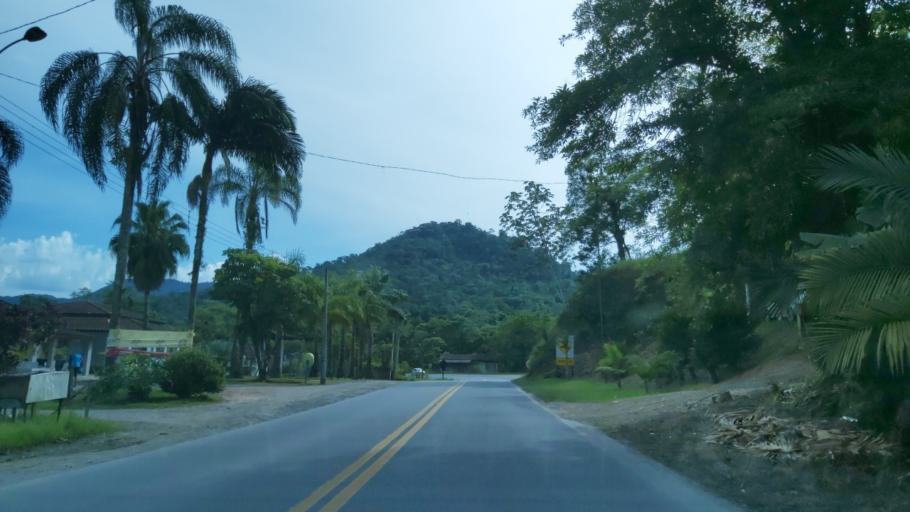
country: BR
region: Sao Paulo
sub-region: Miracatu
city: Miracatu
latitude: -24.0649
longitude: -47.5930
